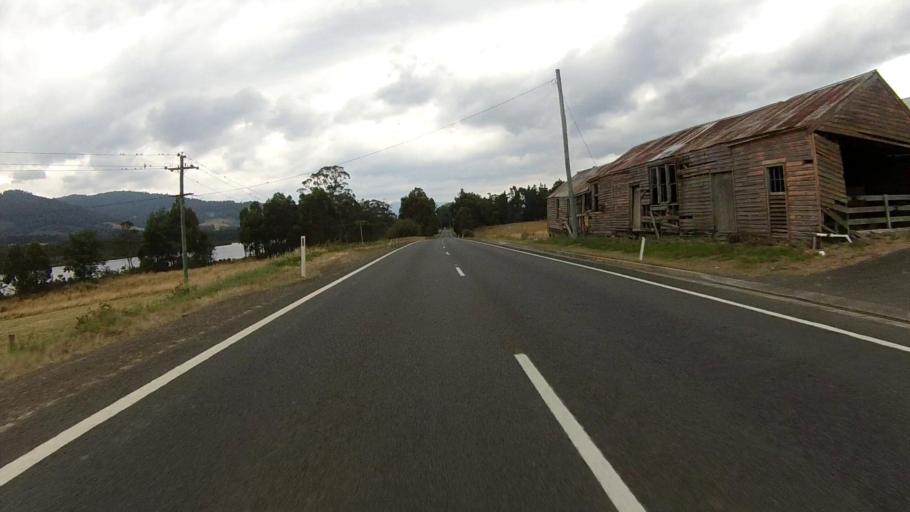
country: AU
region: Tasmania
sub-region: Huon Valley
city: Franklin
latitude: -43.0832
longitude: 147.0306
